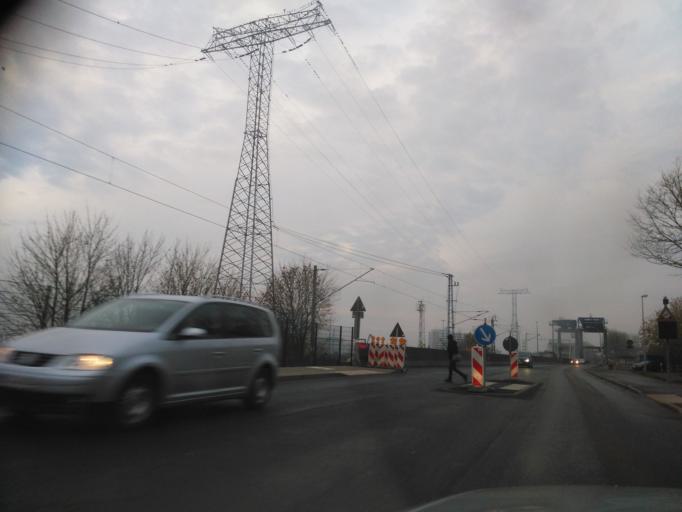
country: DE
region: Mecklenburg-Vorpommern
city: Altefahr
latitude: 54.3087
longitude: 13.1141
